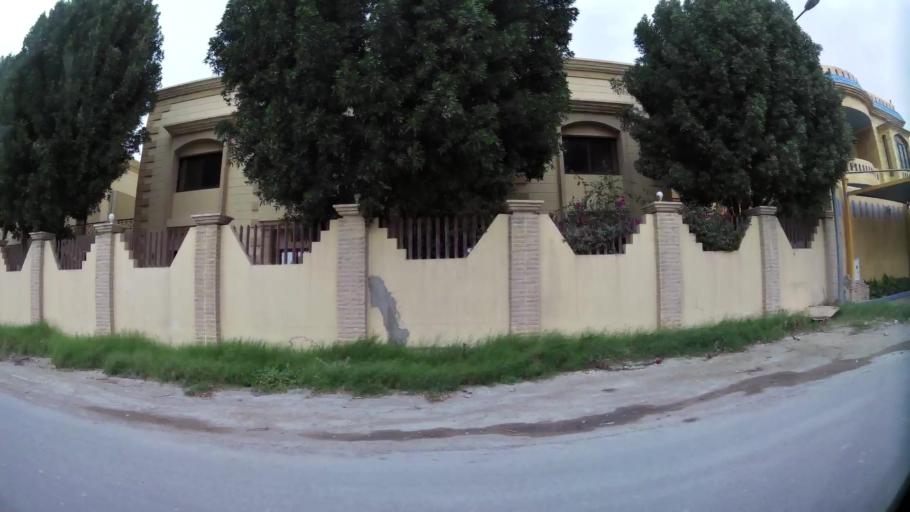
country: QA
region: Baladiyat ad Dawhah
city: Doha
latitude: 25.2466
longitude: 51.5404
